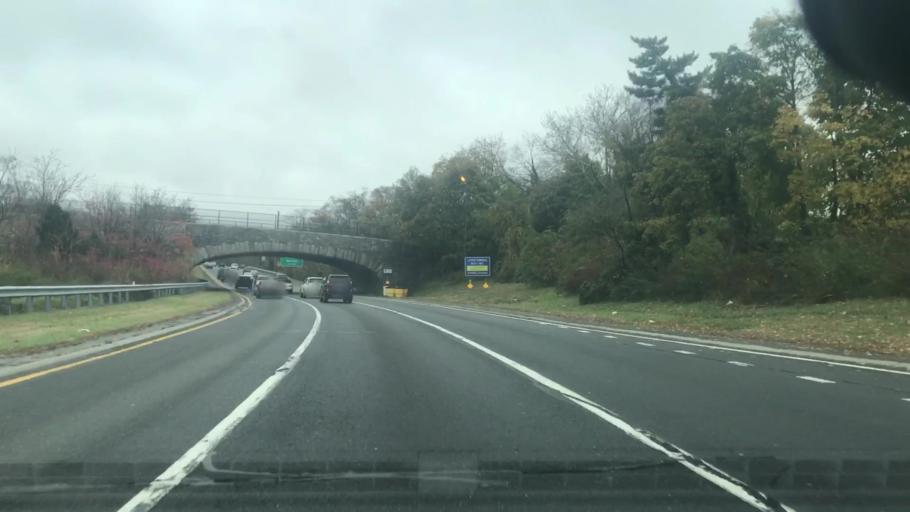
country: US
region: New York
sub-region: Nassau County
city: North Merrick
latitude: 40.6930
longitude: -73.5499
